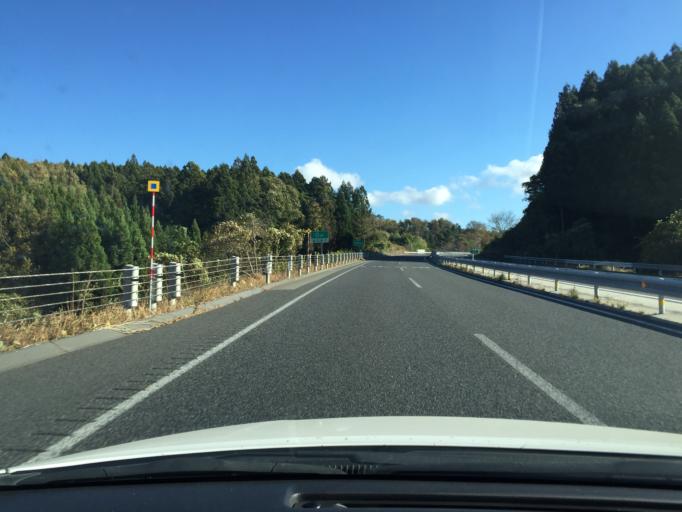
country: JP
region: Fukushima
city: Funehikimachi-funehiki
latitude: 37.4226
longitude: 140.5574
